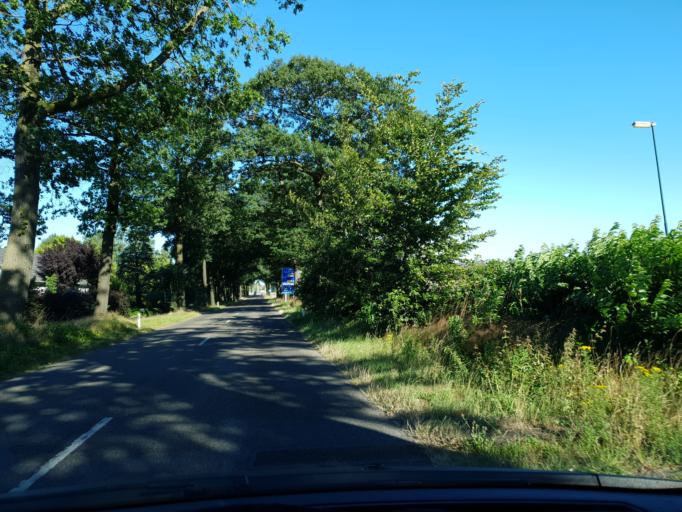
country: NL
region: North Brabant
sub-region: Gemeente Zundert
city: Zundert
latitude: 51.4755
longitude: 4.6457
